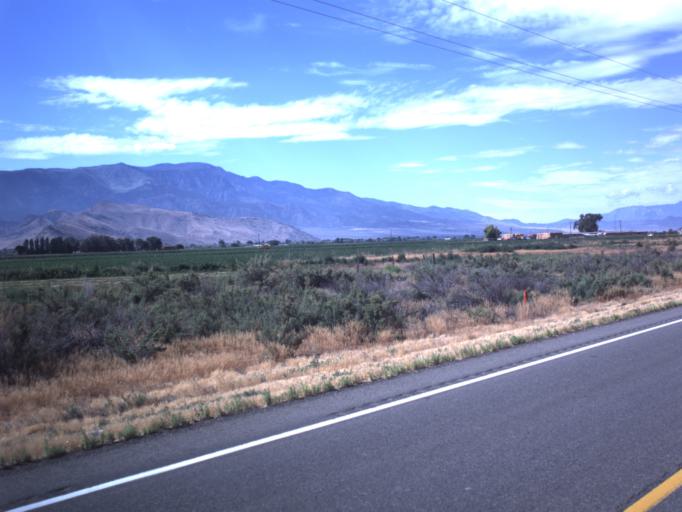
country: US
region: Utah
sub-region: Sevier County
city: Richfield
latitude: 38.8065
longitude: -112.0222
